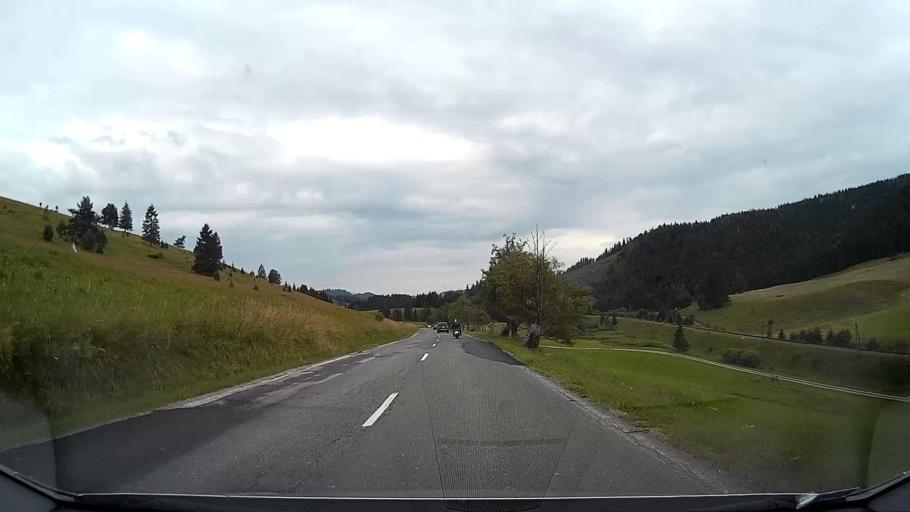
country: SK
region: Kosicky
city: Dobsina
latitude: 48.8598
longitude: 20.2186
